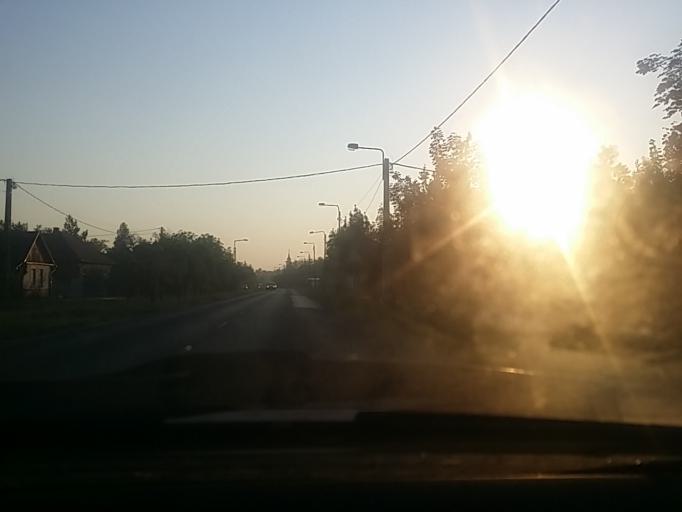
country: HU
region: Pest
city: Szentmartonkata
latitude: 47.4502
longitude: 19.6959
